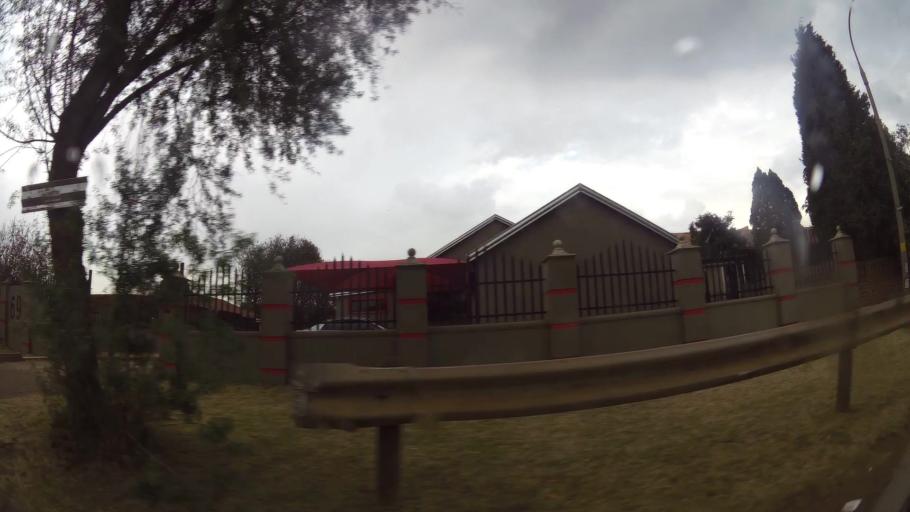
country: ZA
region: Gauteng
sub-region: Ekurhuleni Metropolitan Municipality
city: Germiston
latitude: -26.3759
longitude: 28.1202
